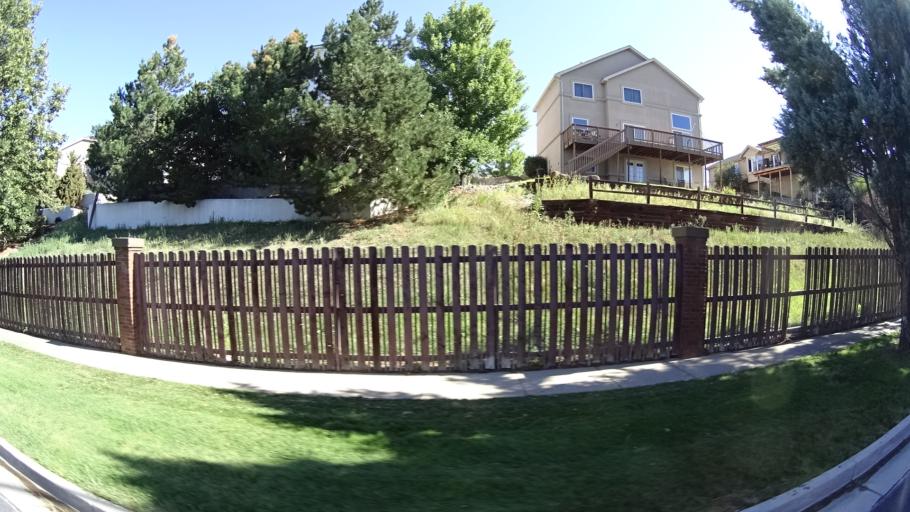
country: US
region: Colorado
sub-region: El Paso County
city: Cimarron Hills
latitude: 38.9223
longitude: -104.7443
